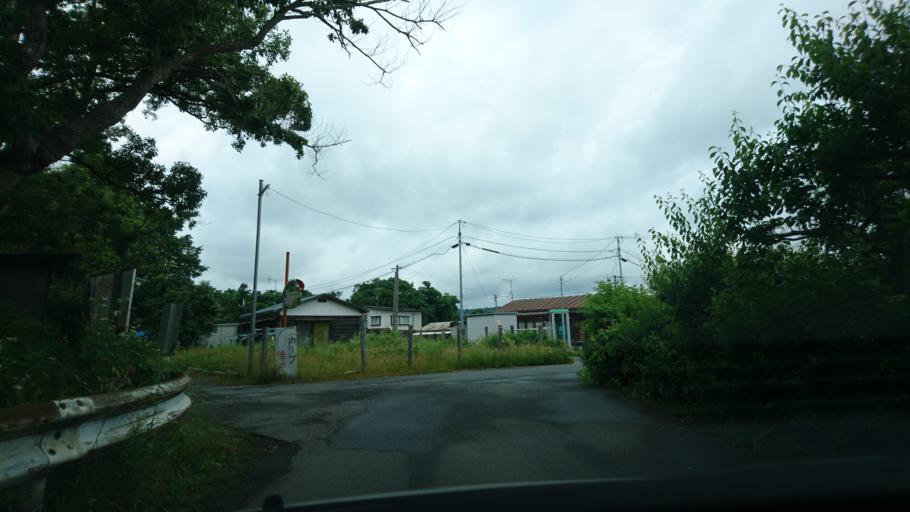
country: JP
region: Iwate
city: Ichinoseki
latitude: 38.9306
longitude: 141.1098
